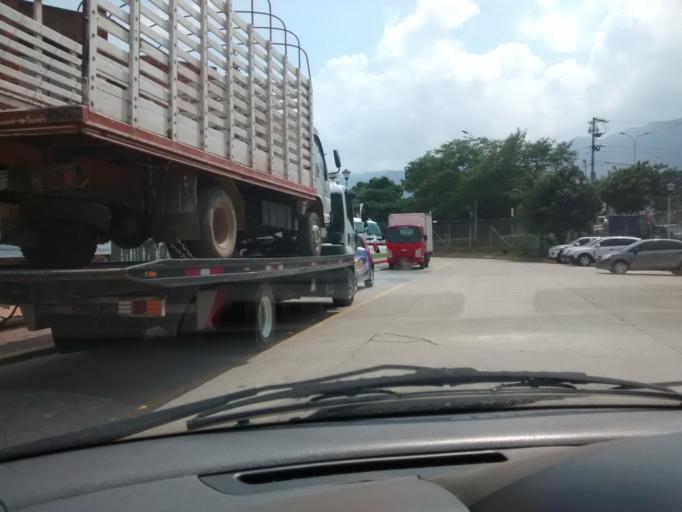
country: CO
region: Santander
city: Giron
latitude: 7.0830
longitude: -73.1683
